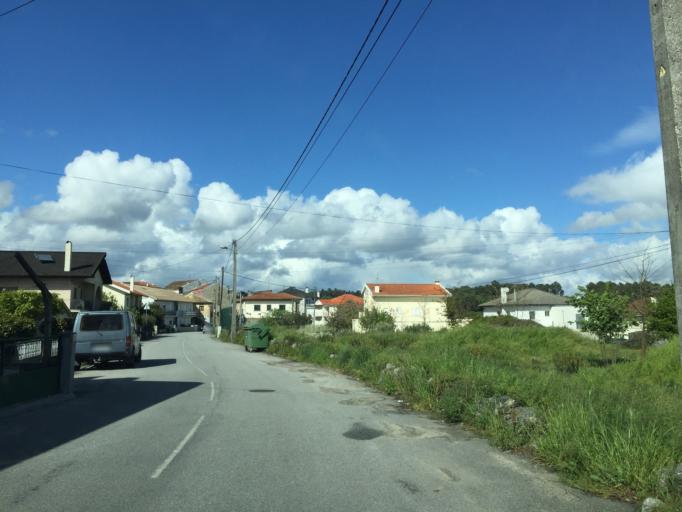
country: PT
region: Viseu
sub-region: Viseu
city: Abraveses
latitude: 40.6623
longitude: -7.9391
